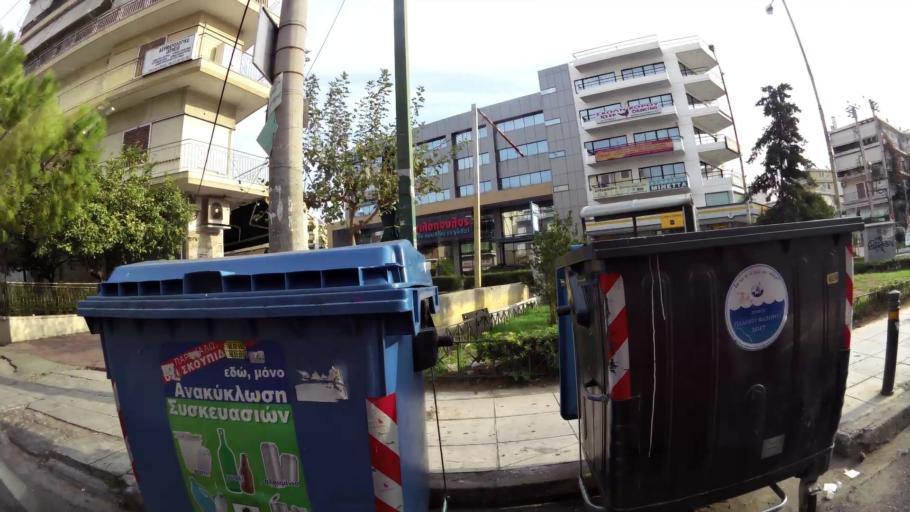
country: GR
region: Attica
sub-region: Nomarchia Athinas
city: Palaio Faliro
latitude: 37.9304
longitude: 23.7022
